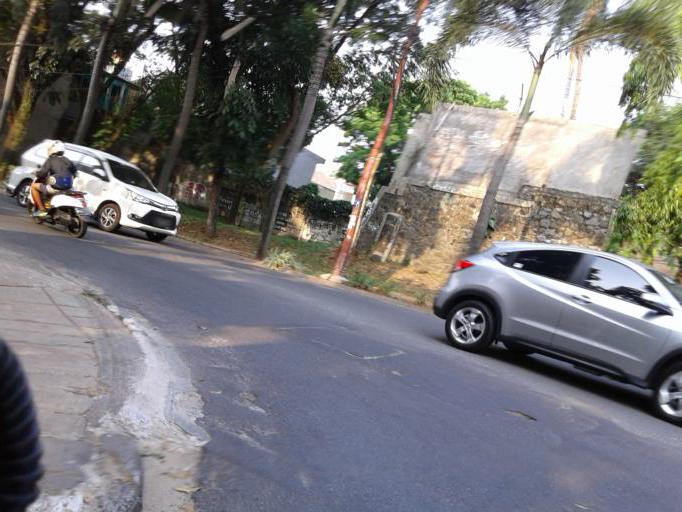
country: ID
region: Banten
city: South Tangerang
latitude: -6.2829
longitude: 106.7081
